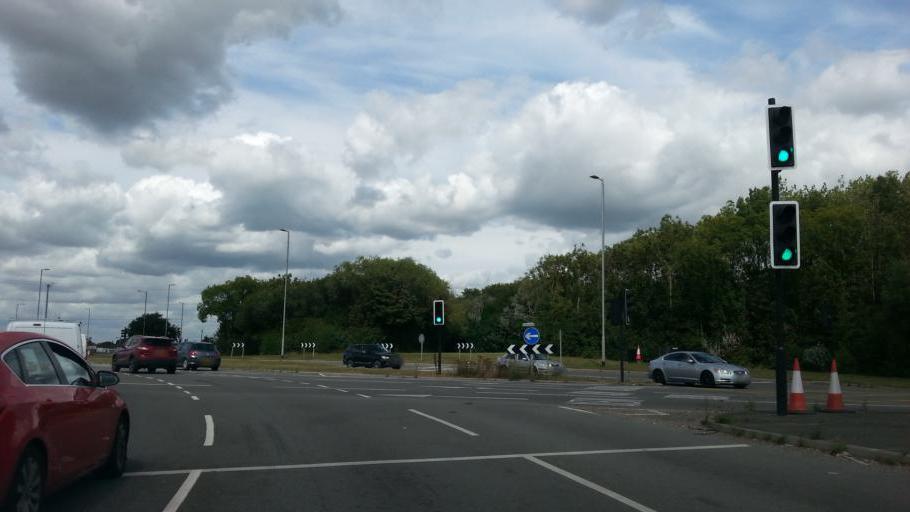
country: GB
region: England
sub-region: Essex
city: South Benfleet
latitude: 51.5659
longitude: 0.5419
